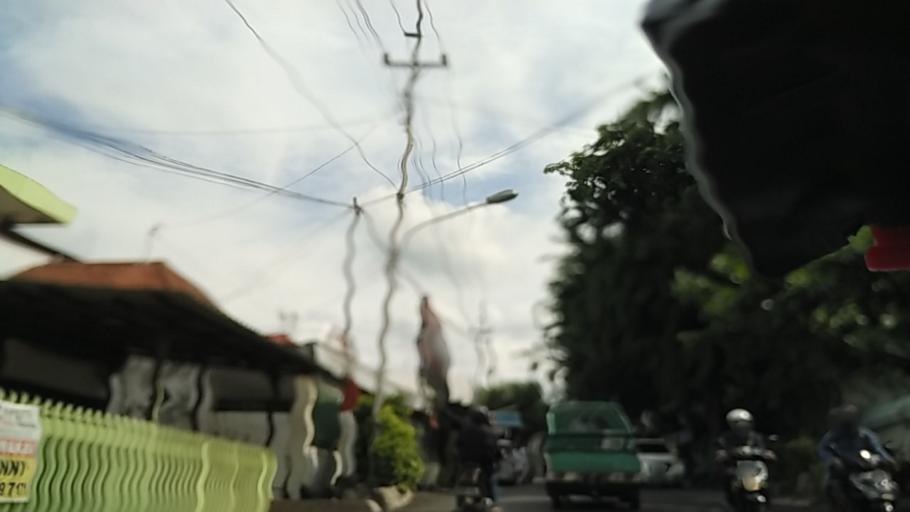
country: ID
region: Central Java
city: Semarang
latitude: -7.0091
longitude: 110.4267
